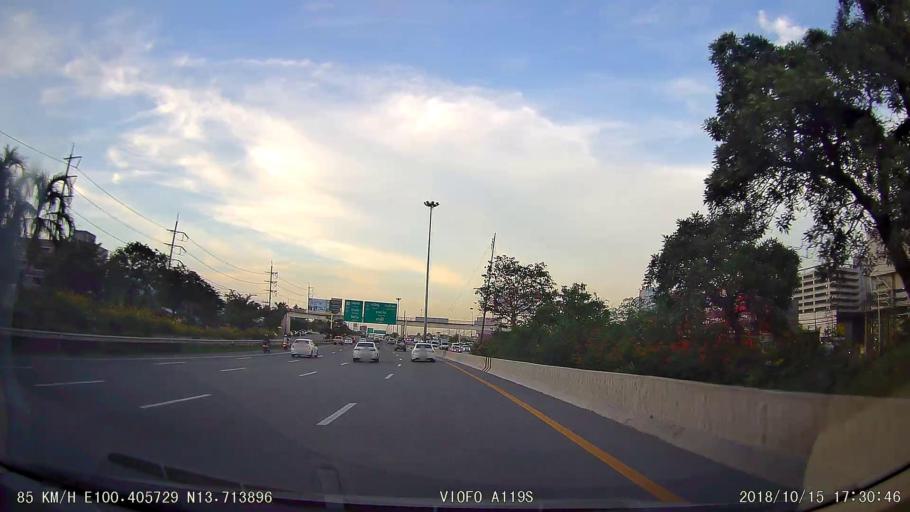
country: TH
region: Bangkok
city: Bang Khae
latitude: 13.7140
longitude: 100.4057
